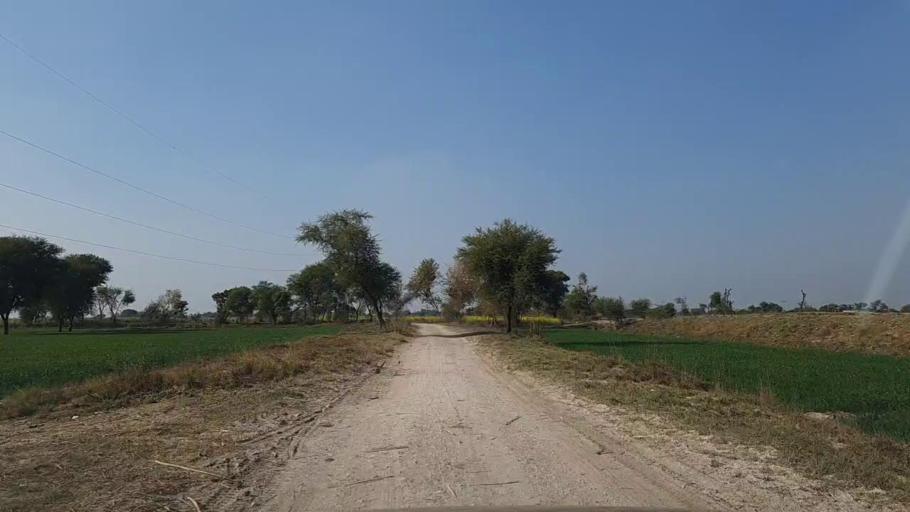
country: PK
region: Sindh
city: Daur
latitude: 26.3843
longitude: 68.3268
